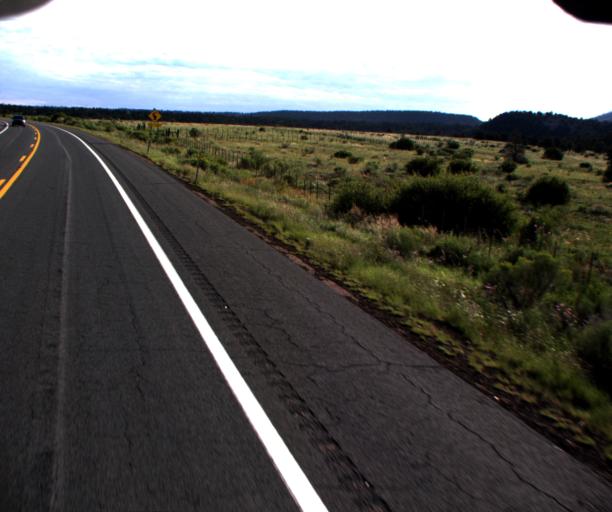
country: US
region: Arizona
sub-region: Apache County
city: Eagar
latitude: 33.9825
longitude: -109.1905
